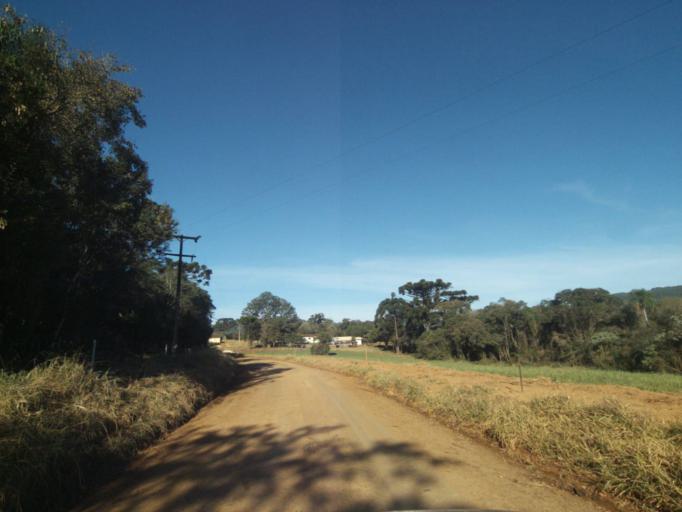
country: BR
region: Parana
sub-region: Tibagi
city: Tibagi
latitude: -24.5409
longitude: -50.5005
